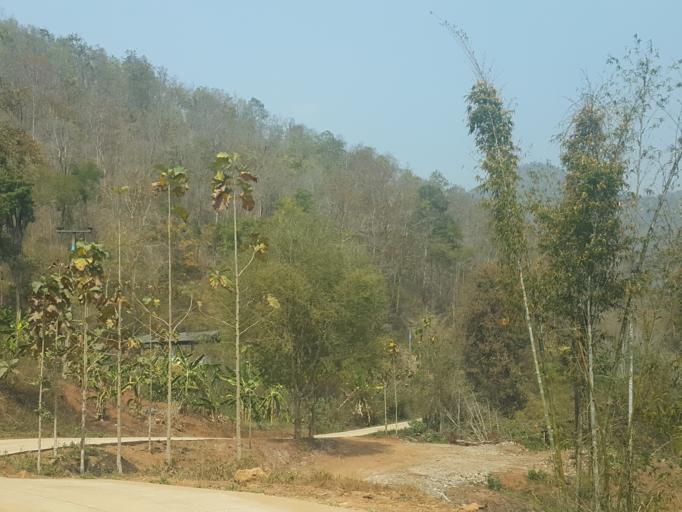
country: TH
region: Chiang Mai
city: Hang Dong
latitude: 18.7478
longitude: 98.8259
